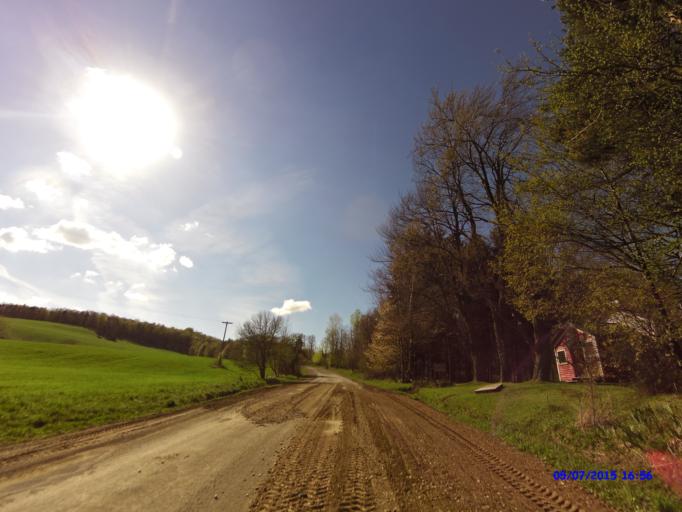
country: US
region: New York
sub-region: Cattaraugus County
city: Little Valley
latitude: 42.3022
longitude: -78.7575
